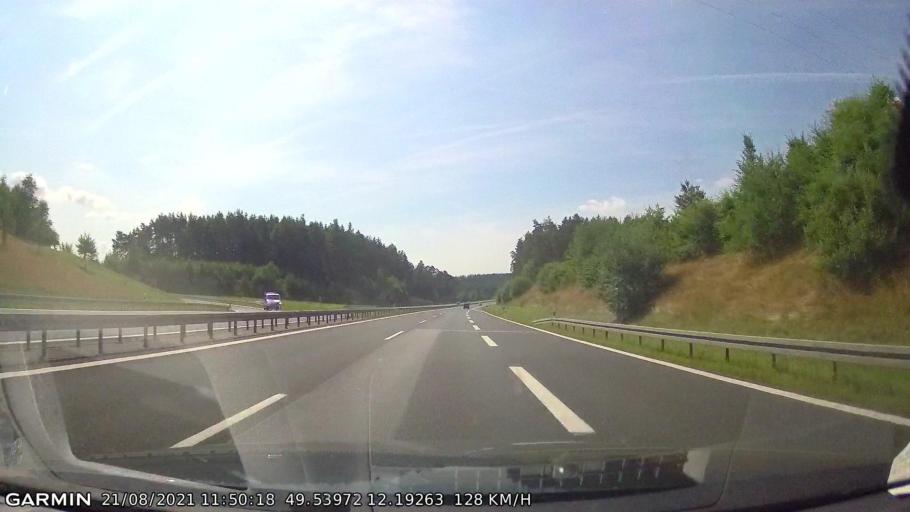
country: DE
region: Bavaria
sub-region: Upper Palatinate
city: Wernberg-Koblitz
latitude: 49.5396
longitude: 12.1926
